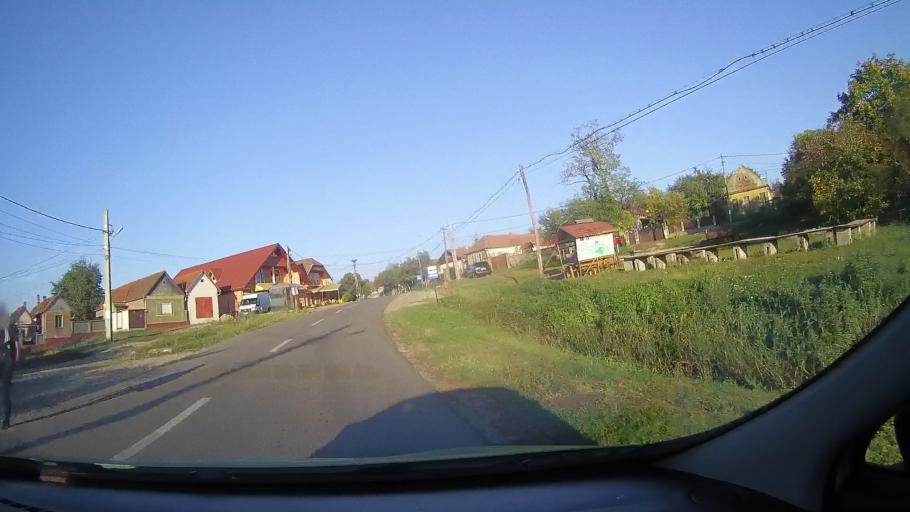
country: RO
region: Bihor
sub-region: Comuna Cetariu
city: Cetariu
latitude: 47.1371
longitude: 21.9954
